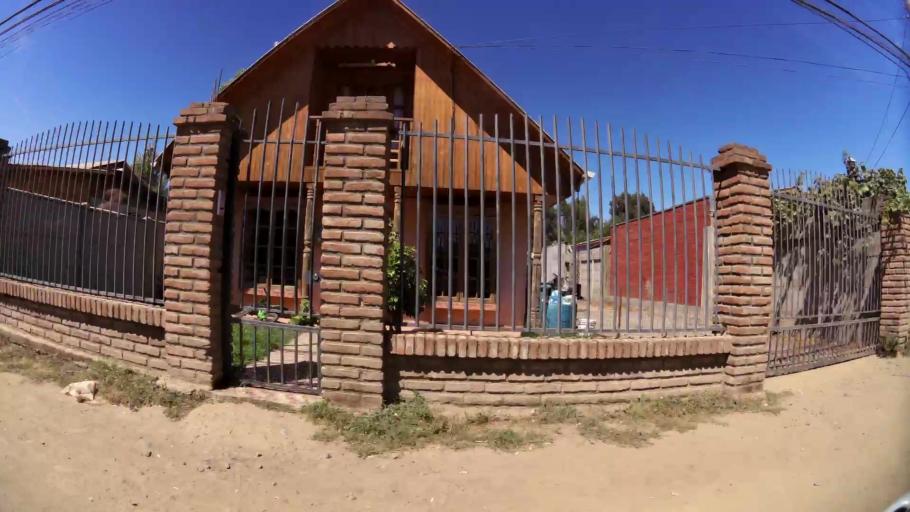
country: CL
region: O'Higgins
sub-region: Provincia de Colchagua
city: Chimbarongo
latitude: -34.5673
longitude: -70.9934
